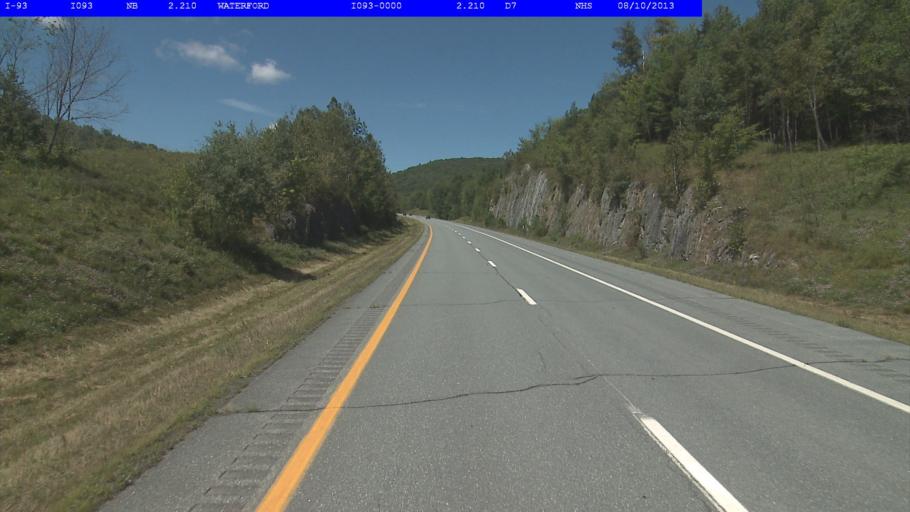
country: US
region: Vermont
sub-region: Caledonia County
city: Saint Johnsbury
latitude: 44.3727
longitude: -71.9071
